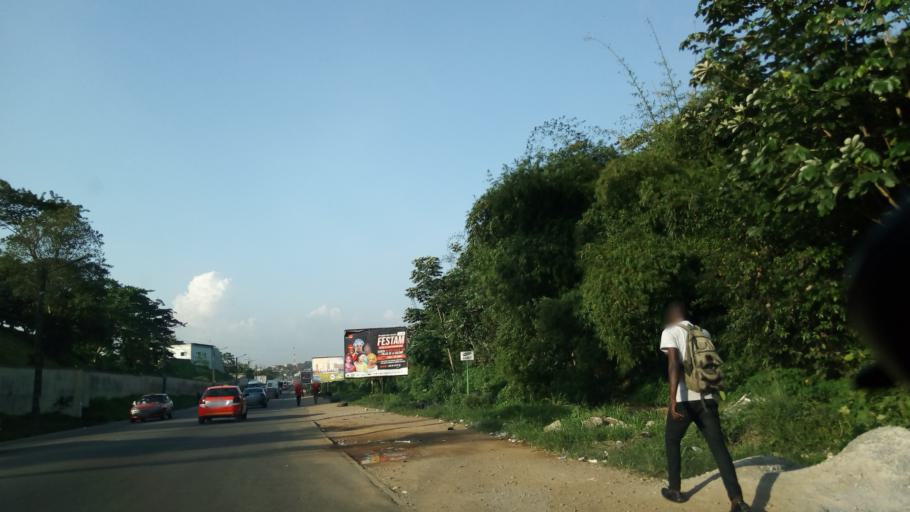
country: CI
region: Lagunes
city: Abobo
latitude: 5.3802
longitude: -4.0067
